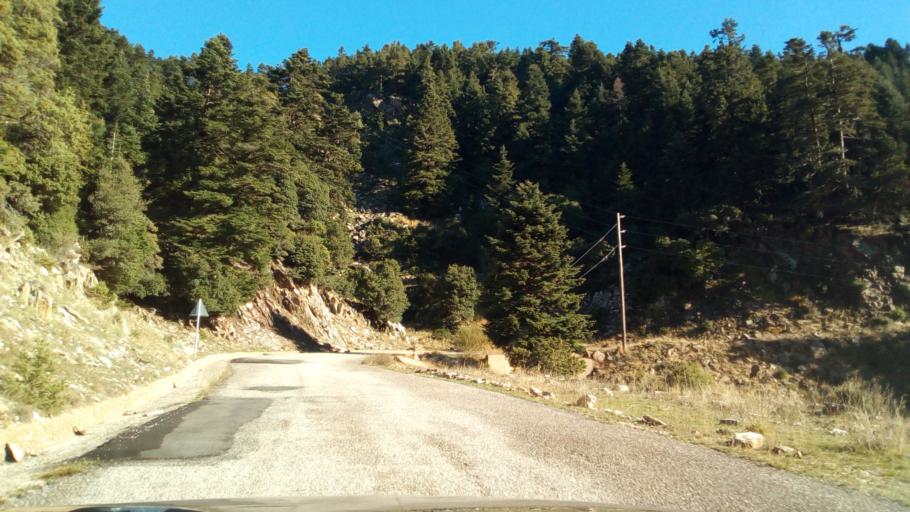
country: GR
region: West Greece
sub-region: Nomos Aitolias kai Akarnanias
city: Nafpaktos
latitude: 38.5288
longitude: 21.8458
